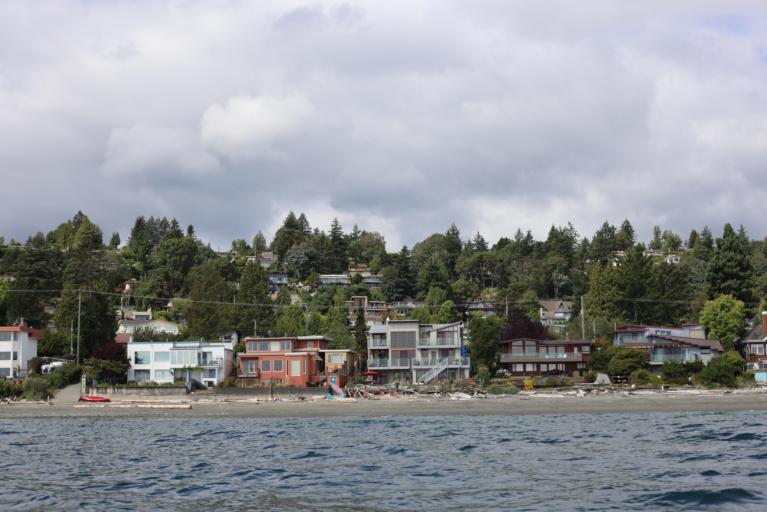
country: CA
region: British Columbia
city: Victoria
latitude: 48.5200
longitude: -123.3646
